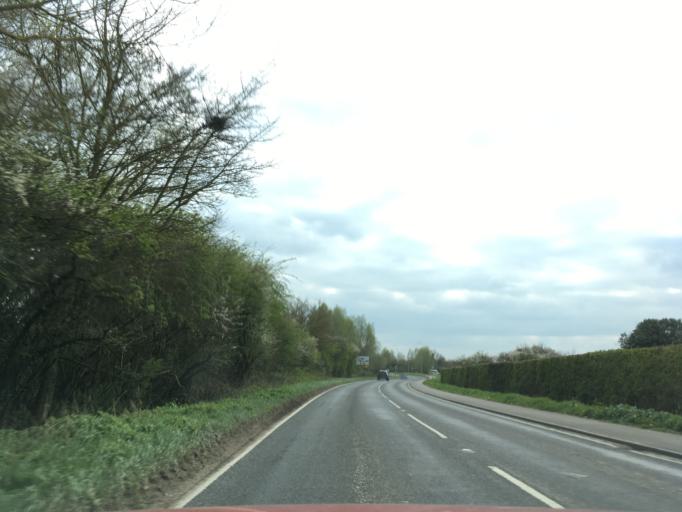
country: GB
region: England
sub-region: Oxfordshire
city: North Leigh
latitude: 51.8001
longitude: -1.4590
